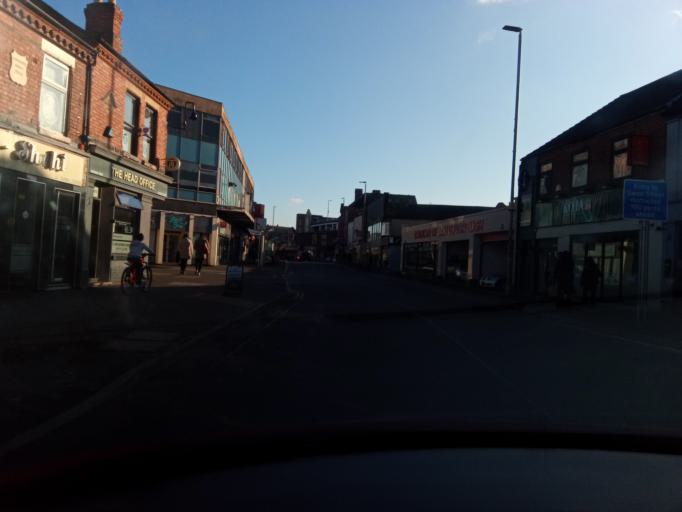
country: GB
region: England
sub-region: Leicestershire
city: Loughborough
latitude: 52.7734
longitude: -1.2090
